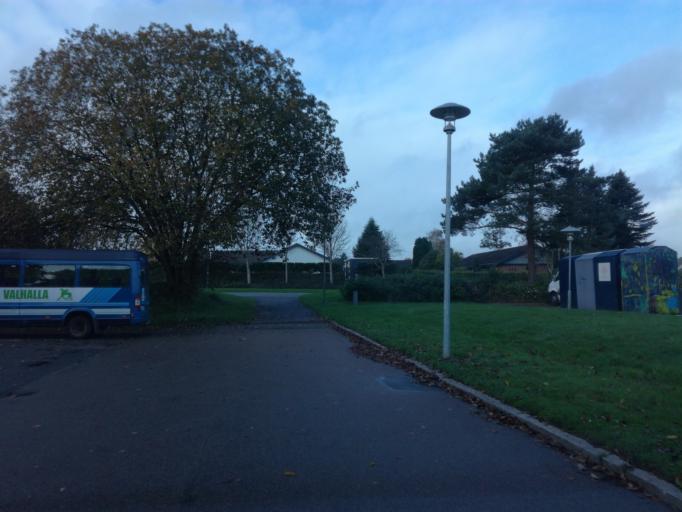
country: DK
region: South Denmark
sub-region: Vejle Kommune
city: Vejle
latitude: 55.6870
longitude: 9.5514
